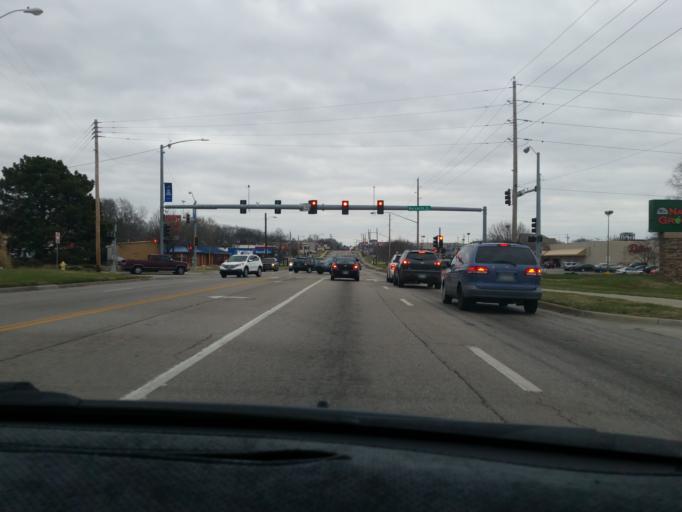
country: US
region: Kansas
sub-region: Douglas County
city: Lawrence
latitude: 38.9428
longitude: -95.2510
